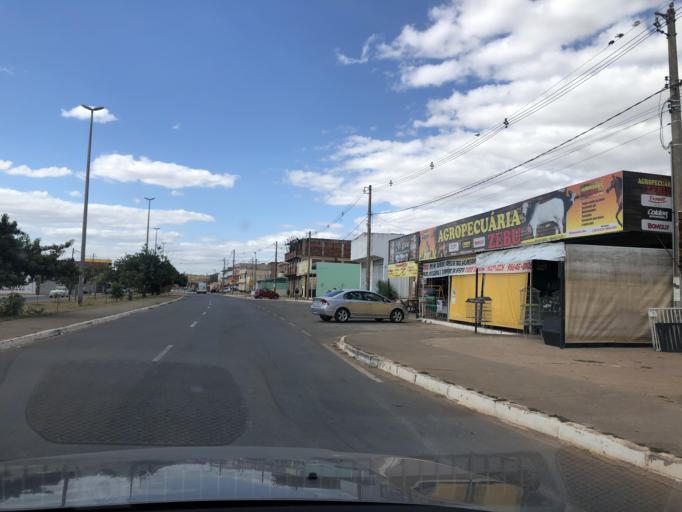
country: BR
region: Federal District
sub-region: Brasilia
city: Brasilia
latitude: -15.8873
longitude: -48.1479
